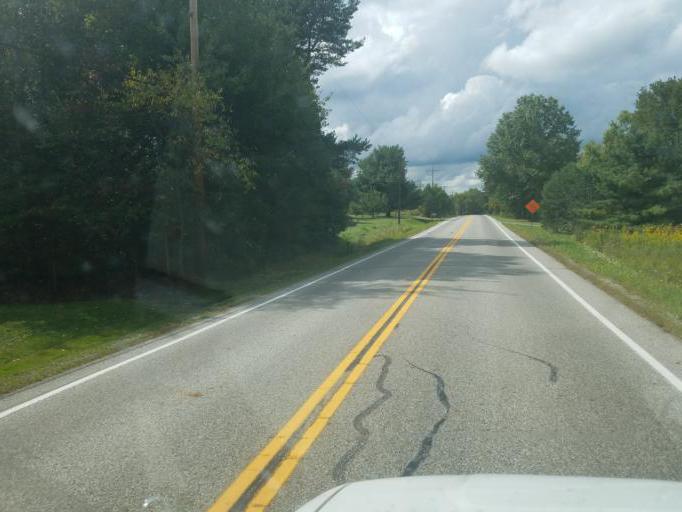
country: US
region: Ohio
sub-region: Geauga County
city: Burton
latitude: 41.4536
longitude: -81.1248
